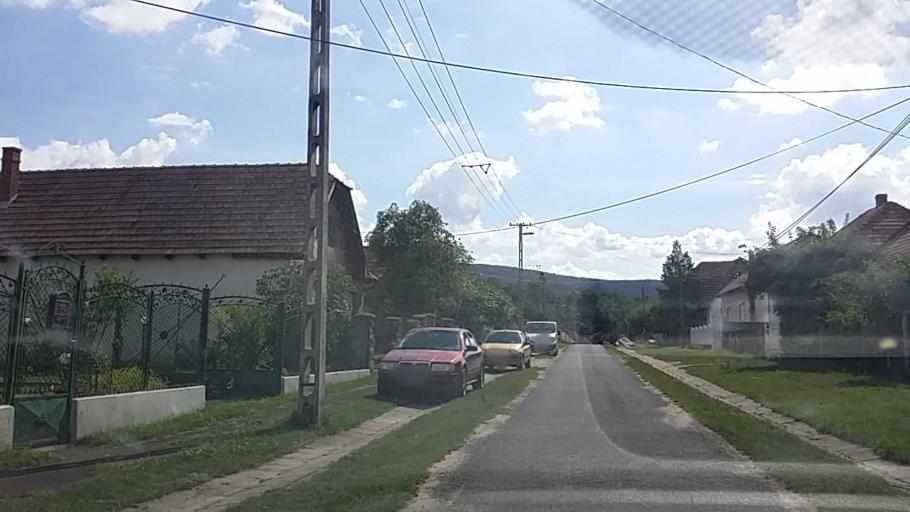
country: SK
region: Nitriansky
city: Sahy
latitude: 48.0531
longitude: 18.9999
